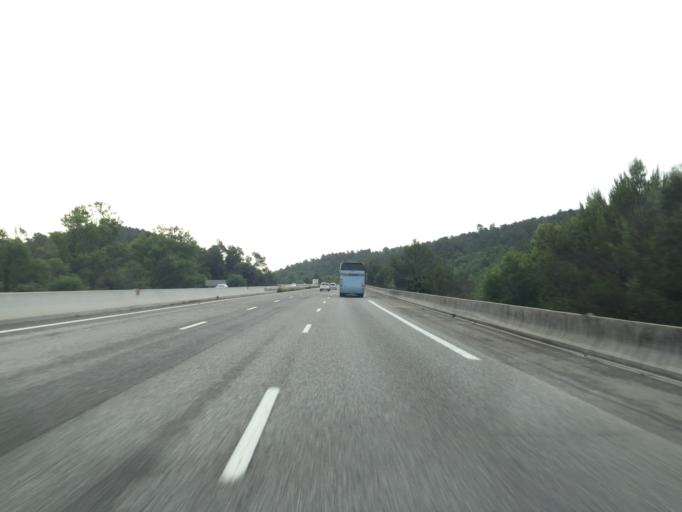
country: FR
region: Provence-Alpes-Cote d'Azur
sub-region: Departement du Var
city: Camps-la-Source
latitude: 43.4186
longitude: 6.1221
